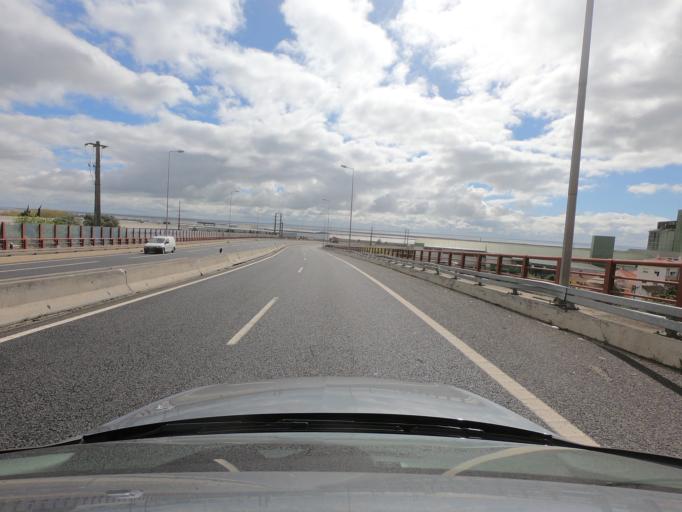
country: PT
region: Lisbon
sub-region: Loures
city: Santa Iria da Azoia
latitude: 38.8460
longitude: -9.0805
